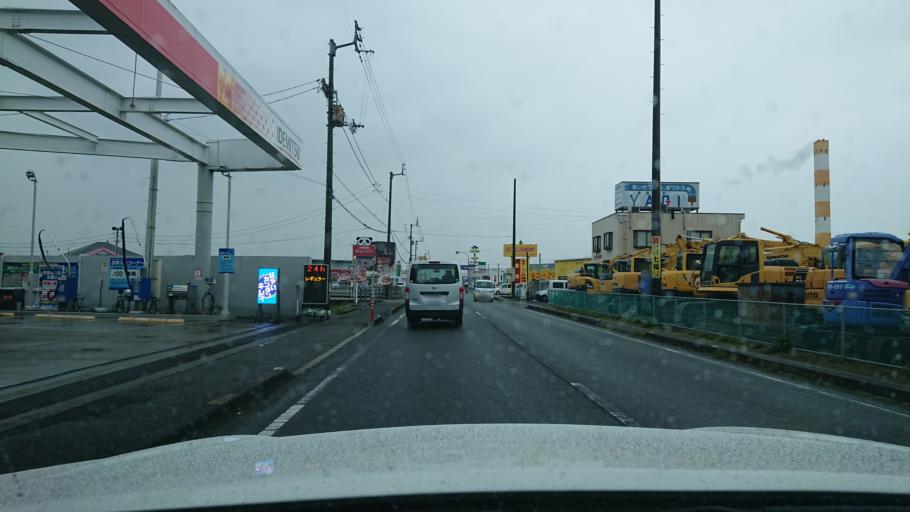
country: JP
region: Tokushima
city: Ishii
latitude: 34.0846
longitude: 134.4961
